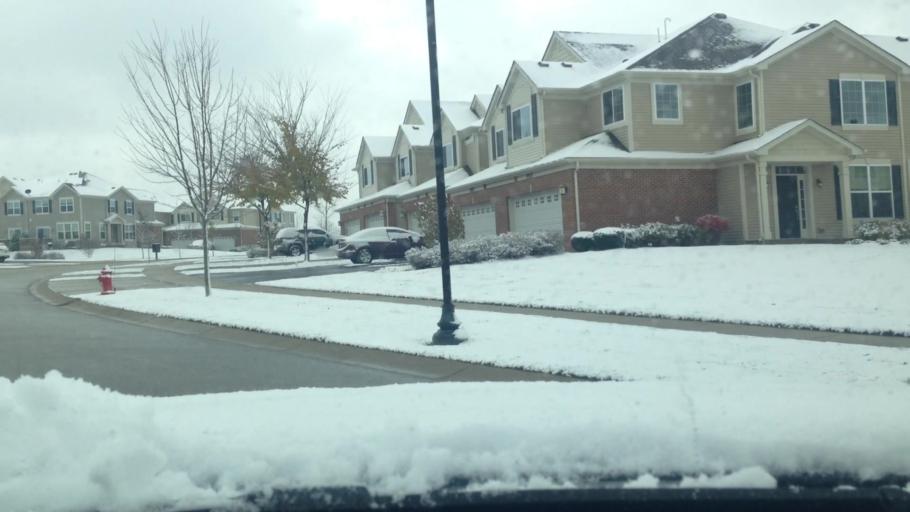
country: US
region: Illinois
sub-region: McHenry County
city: Huntley
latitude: 42.1857
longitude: -88.4281
